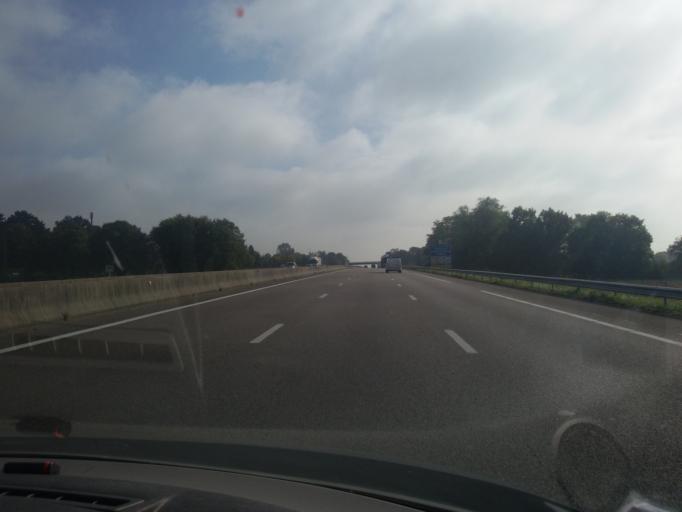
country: FR
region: Haute-Normandie
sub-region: Departement de l'Eure
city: Saint-Pierre-du-Vauvray
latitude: 49.2246
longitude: 1.2100
